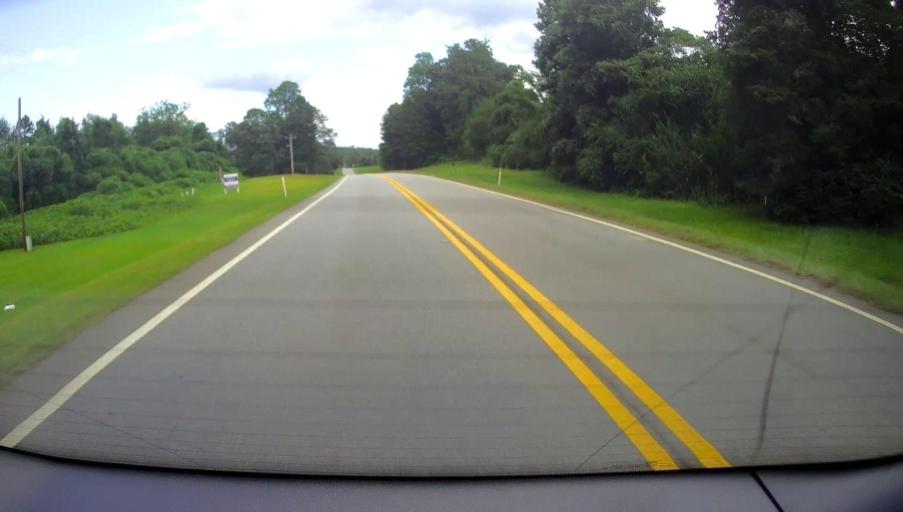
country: US
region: Georgia
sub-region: Bibb County
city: West Point
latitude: 32.8646
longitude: -83.8483
